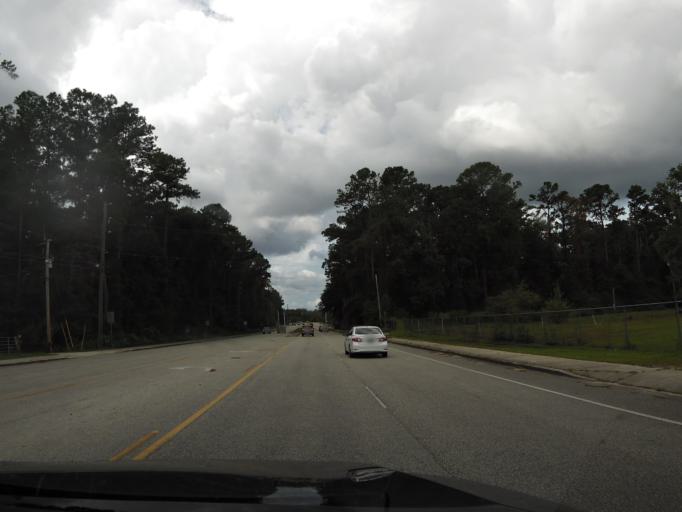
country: US
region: Florida
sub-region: Clay County
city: Lakeside
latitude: 30.1054
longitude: -81.7943
